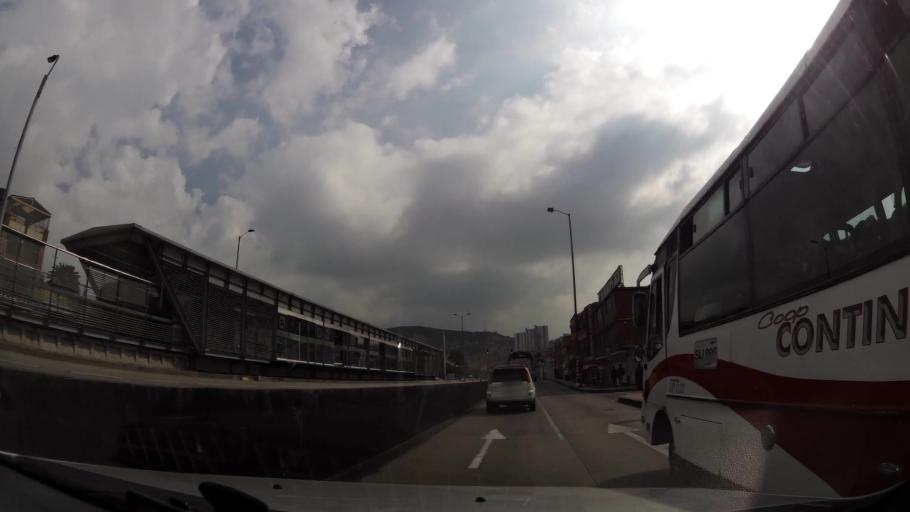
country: CO
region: Bogota D.C.
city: Bogota
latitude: 4.5715
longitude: -74.0987
